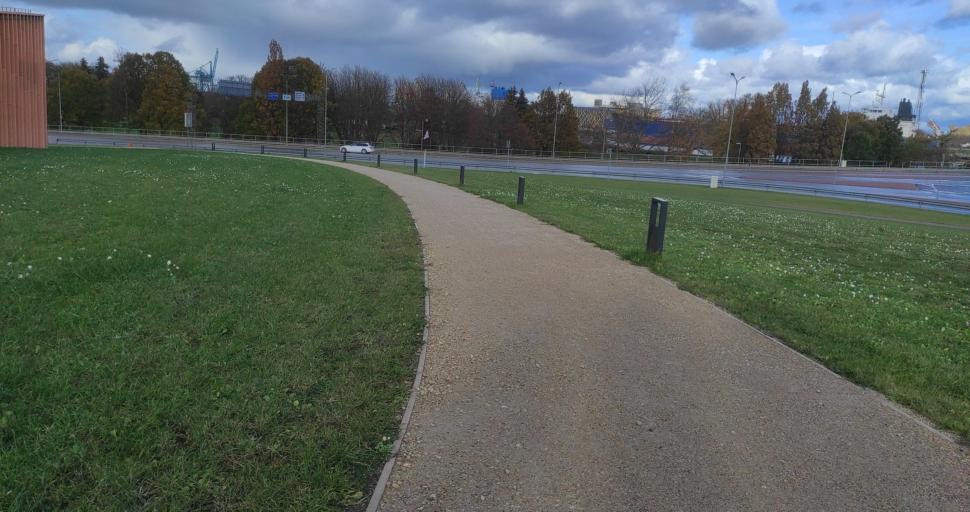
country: LV
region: Ventspils
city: Ventspils
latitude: 57.3866
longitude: 21.5846
